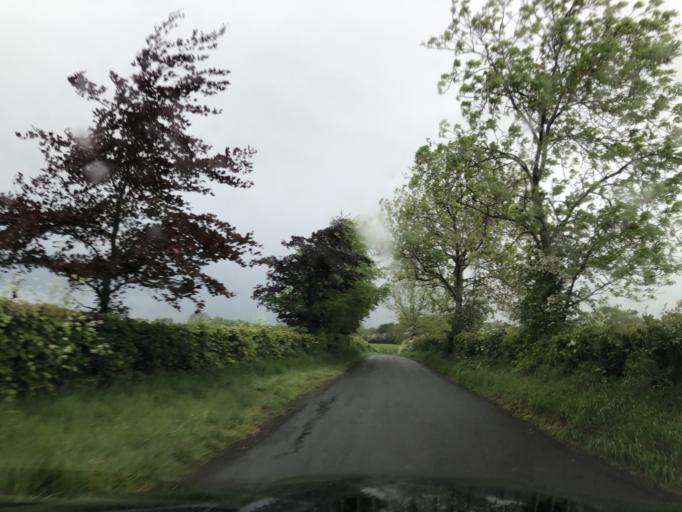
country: GB
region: Northern Ireland
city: Dunloy
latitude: 55.1373
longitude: -6.3737
